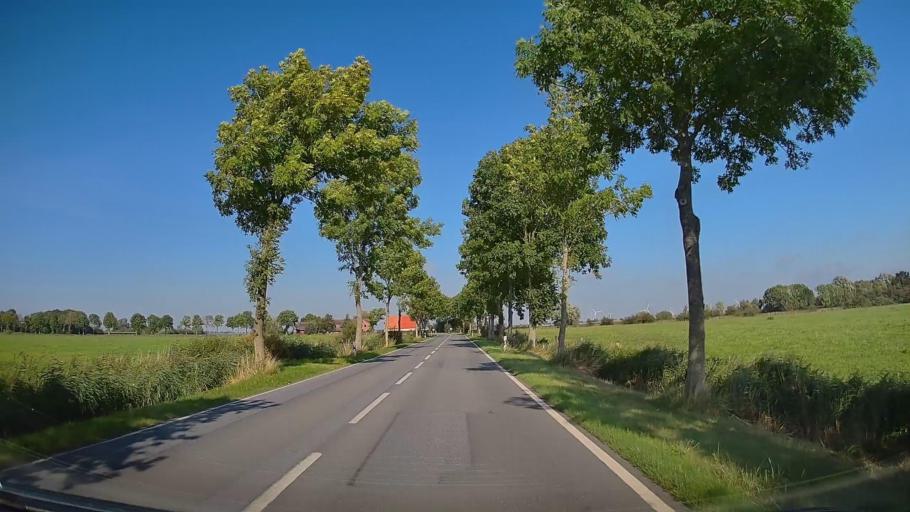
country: DE
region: Lower Saxony
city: Wremen
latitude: 53.6215
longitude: 8.5310
